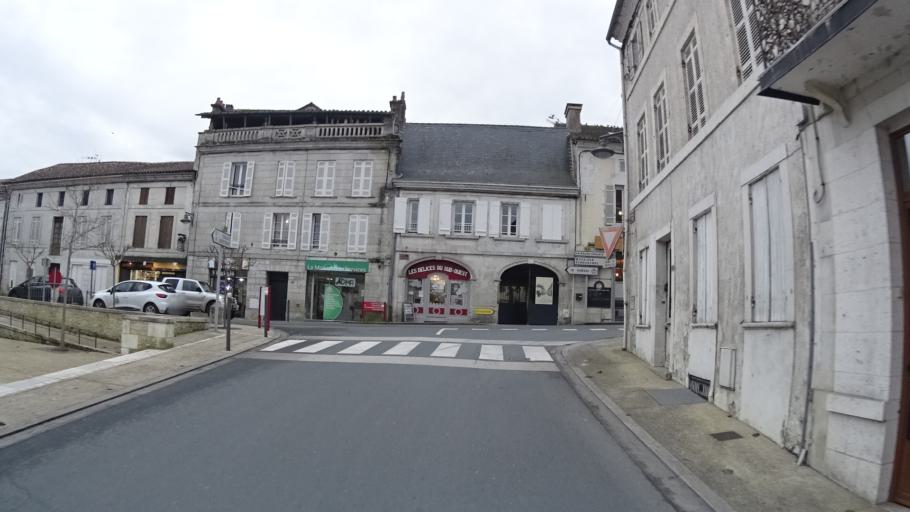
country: FR
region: Aquitaine
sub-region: Departement de la Dordogne
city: Saint-Aulaye
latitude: 45.2032
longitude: 0.1355
